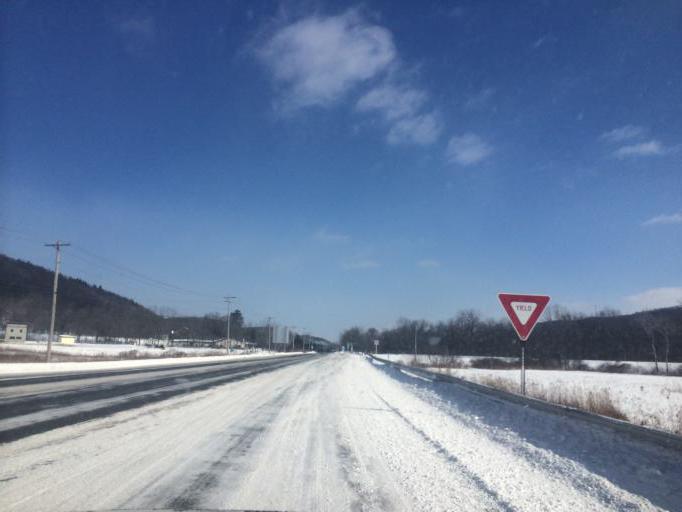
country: US
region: Pennsylvania
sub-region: Centre County
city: Stormstown
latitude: 40.8311
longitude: -78.0125
